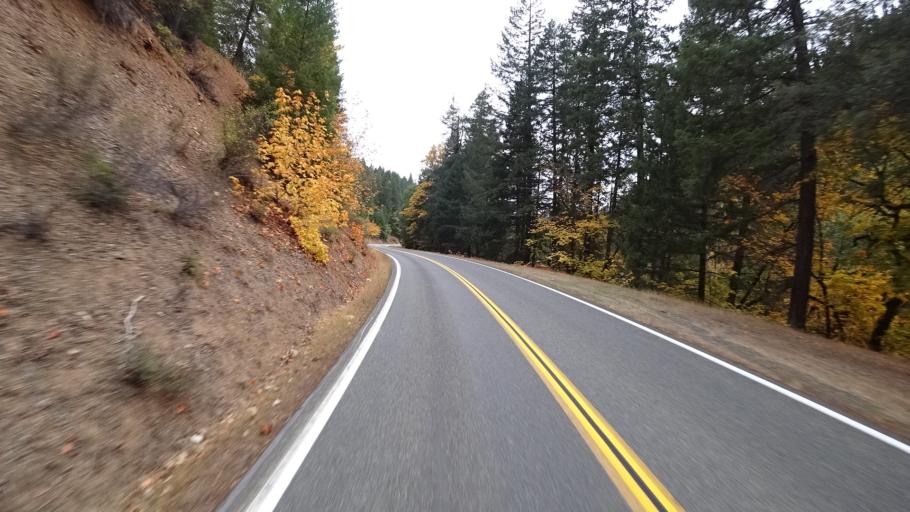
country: US
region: California
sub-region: Siskiyou County
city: Happy Camp
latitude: 41.9065
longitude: -123.4424
